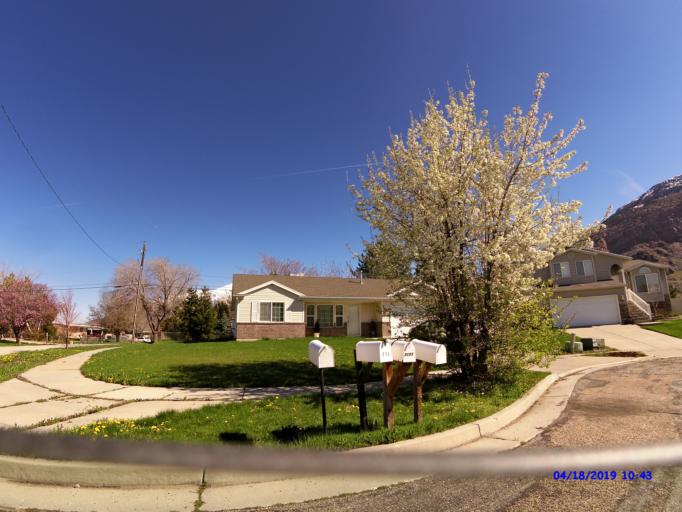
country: US
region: Utah
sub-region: Weber County
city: Harrisville
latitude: 41.2682
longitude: -111.9613
